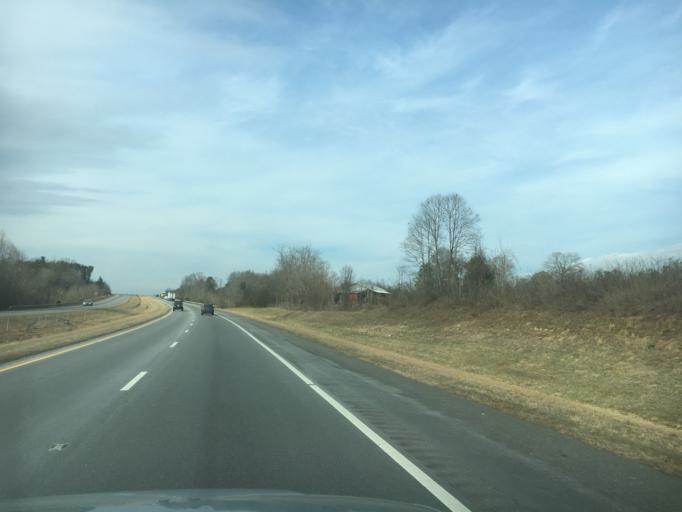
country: US
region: North Carolina
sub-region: Catawba County
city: Newton
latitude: 35.6272
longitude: -81.2910
